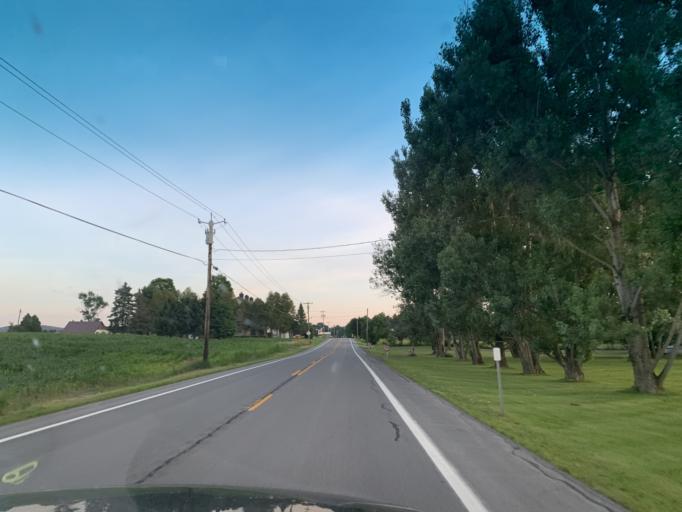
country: US
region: New York
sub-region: Oneida County
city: Chadwicks
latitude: 42.8973
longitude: -75.2445
